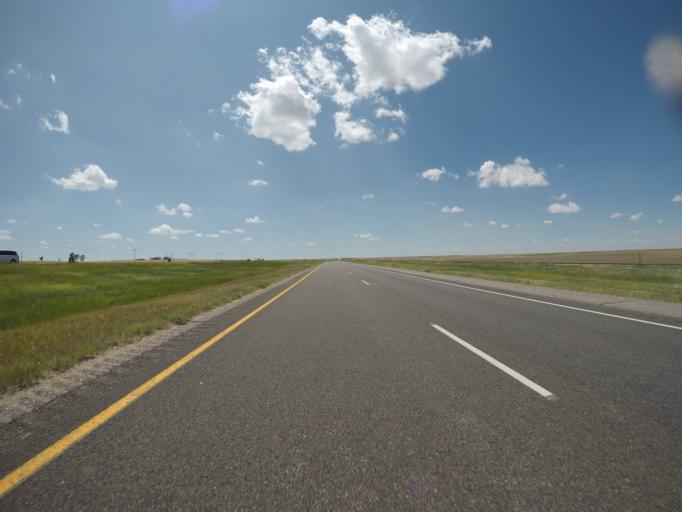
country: US
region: Colorado
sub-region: Lincoln County
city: Hugo
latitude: 39.2871
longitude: -103.1503
